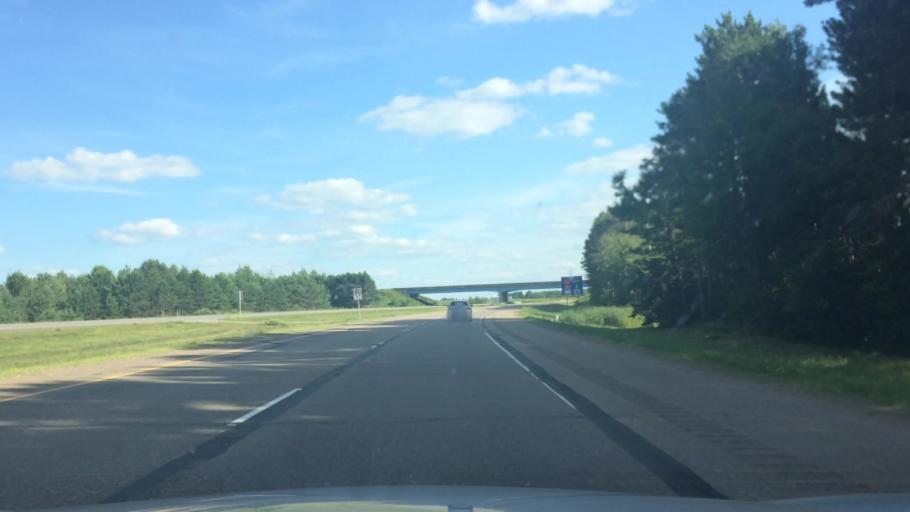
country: US
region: Wisconsin
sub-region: Lincoln County
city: Merrill
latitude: 45.1952
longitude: -89.6477
